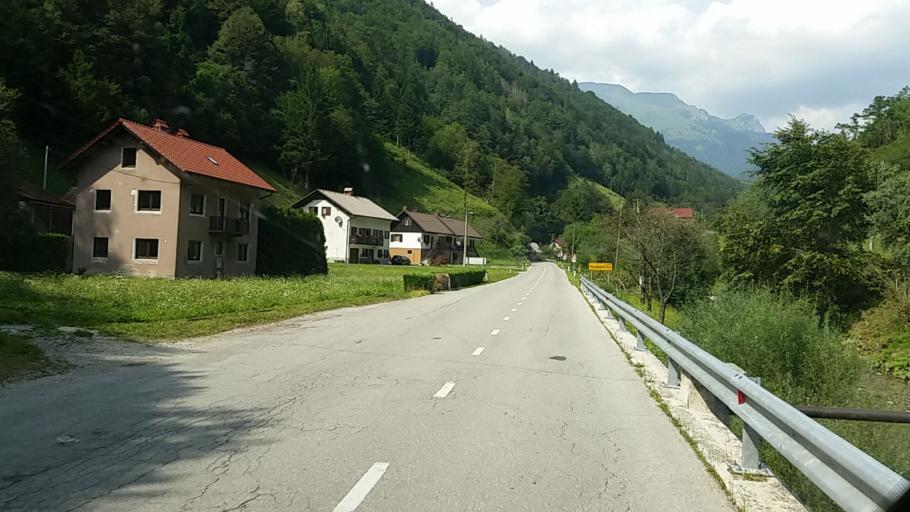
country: SI
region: Cerkno
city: Cerkno
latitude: 46.1777
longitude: 13.9188
